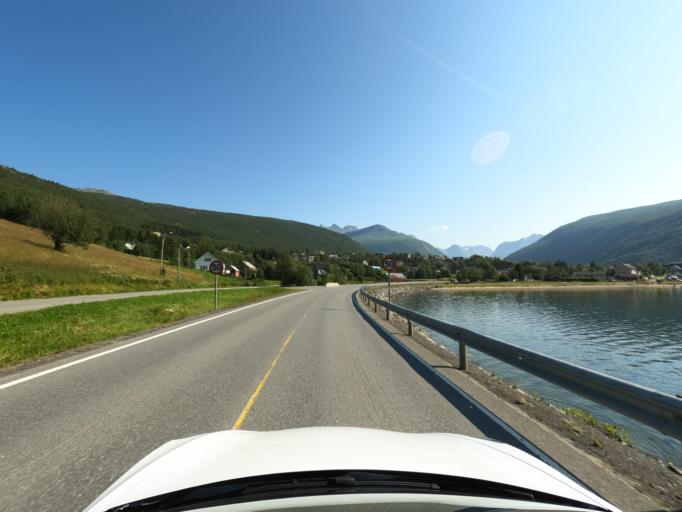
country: NO
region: Nordland
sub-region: Narvik
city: Bjerkvik
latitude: 68.3799
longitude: 17.5968
